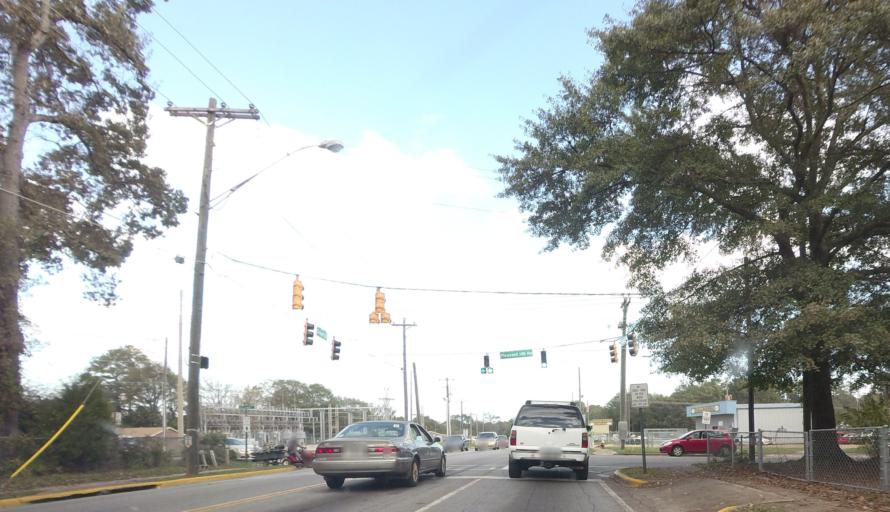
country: US
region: Georgia
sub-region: Houston County
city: Warner Robins
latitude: 32.6263
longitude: -83.6228
